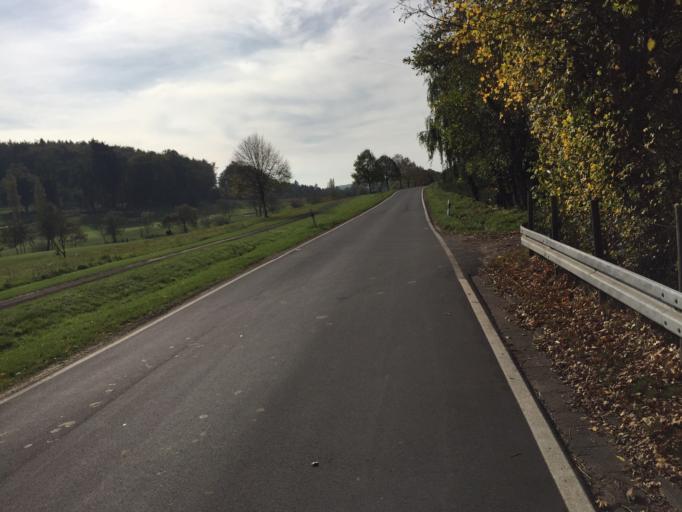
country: DE
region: Hesse
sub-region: Regierungsbezirk Giessen
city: Reiskirchen
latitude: 50.6069
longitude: 8.8634
